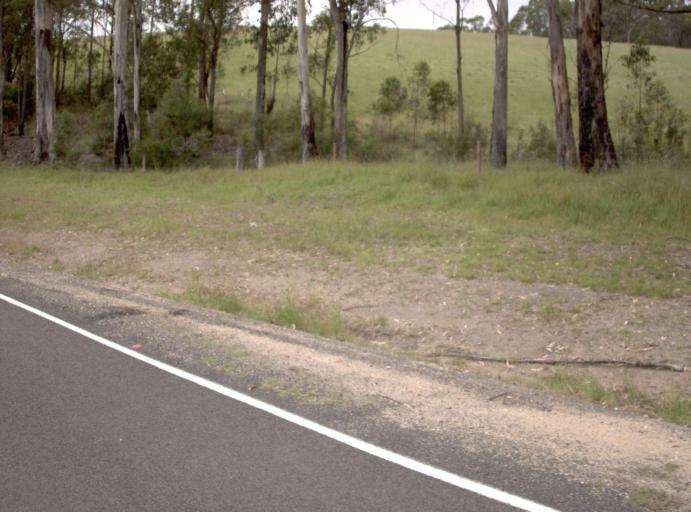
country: AU
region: New South Wales
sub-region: Bombala
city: Bombala
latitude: -37.4407
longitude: 149.1977
